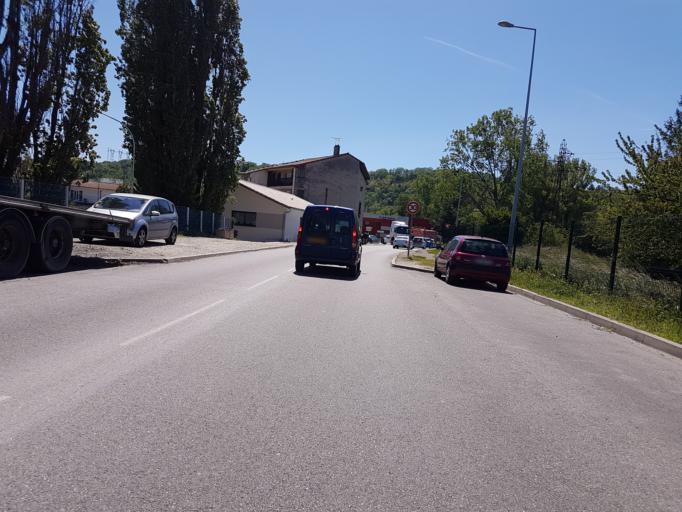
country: FR
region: Rhone-Alpes
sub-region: Departement du Rhone
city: Givors
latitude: 45.5847
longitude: 4.7839
